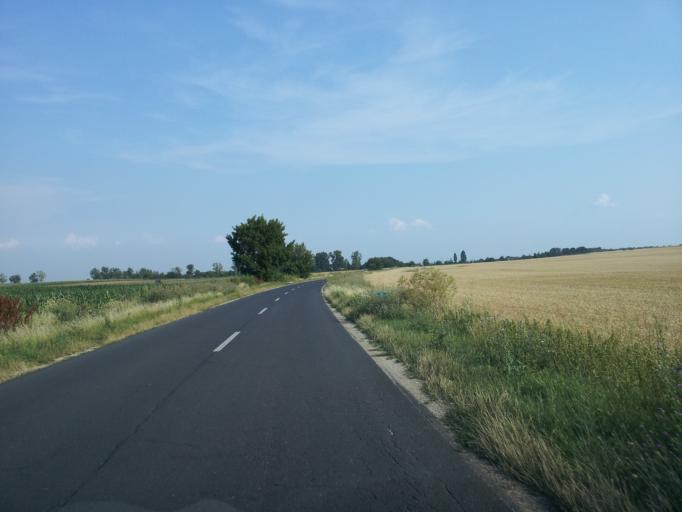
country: HU
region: Veszprem
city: Balatonkenese
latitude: 47.0576
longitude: 18.0849
